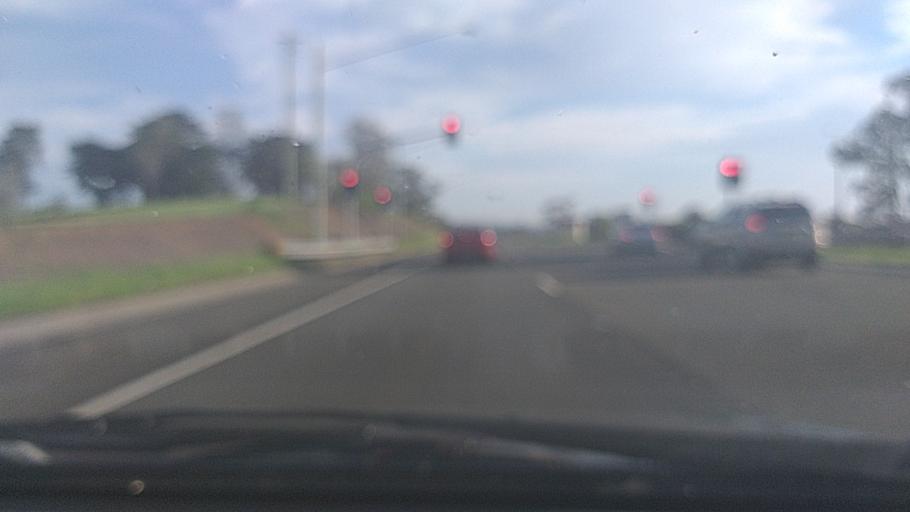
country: AU
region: New South Wales
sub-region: Campbelltown Municipality
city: Glen Alpine
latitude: -34.0893
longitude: 150.8057
